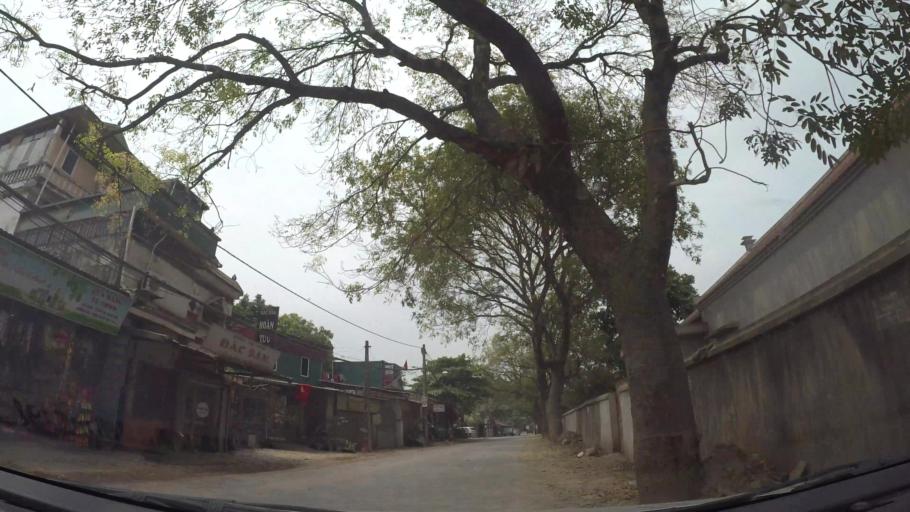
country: VN
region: Ha Noi
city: Cau Dien
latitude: 21.0310
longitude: 105.7395
